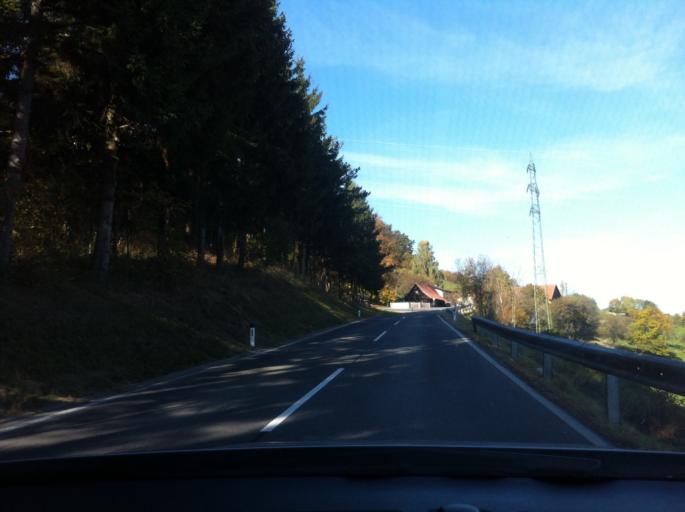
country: AT
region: Lower Austria
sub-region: Politischer Bezirk Neunkirchen
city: Grimmenstein
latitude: 47.6114
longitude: 16.1143
